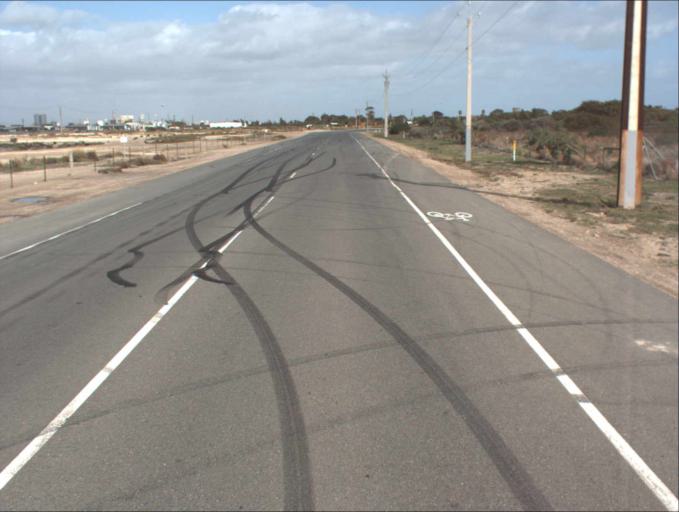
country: AU
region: South Australia
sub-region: Port Adelaide Enfield
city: Birkenhead
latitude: -34.7779
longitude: 138.5015
